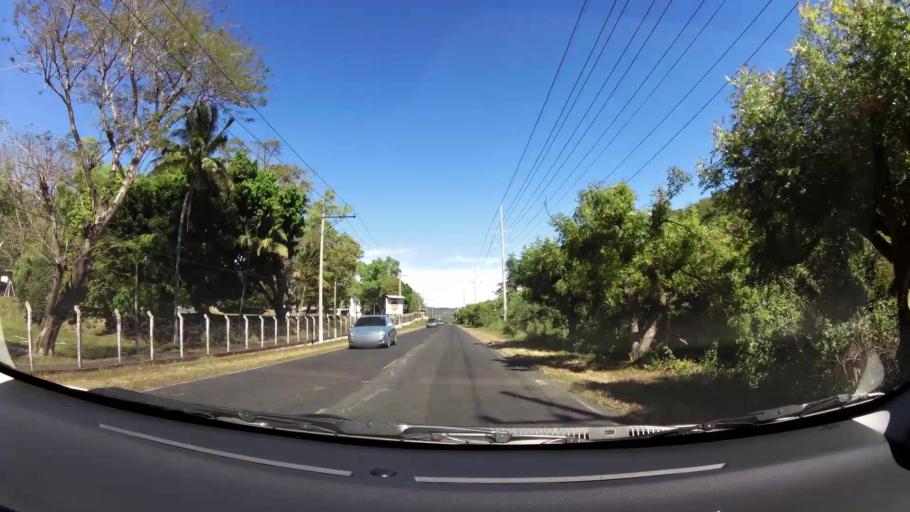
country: SV
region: La Libertad
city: San Juan Opico
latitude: 13.8377
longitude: -89.3596
